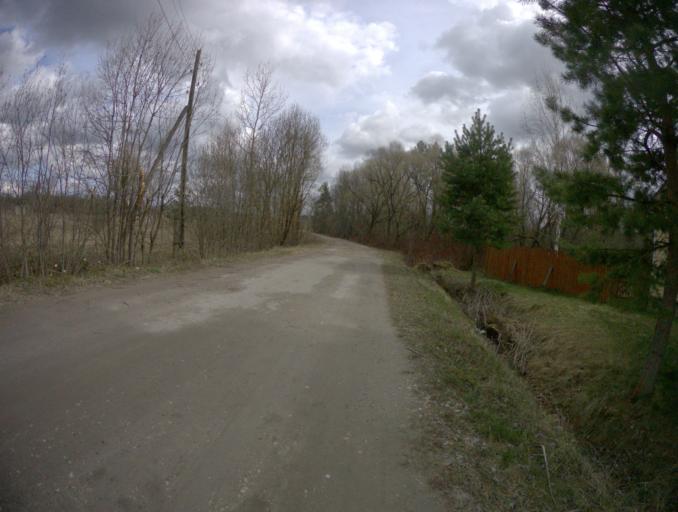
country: RU
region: Vladimir
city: Sudogda
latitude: 56.0755
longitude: 40.7634
